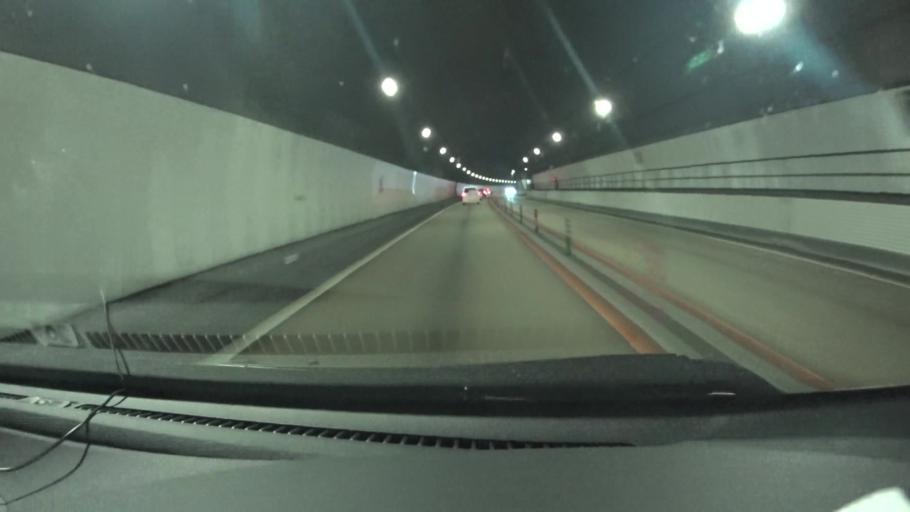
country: JP
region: Kyoto
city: Kameoka
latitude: 35.1375
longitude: 135.4520
